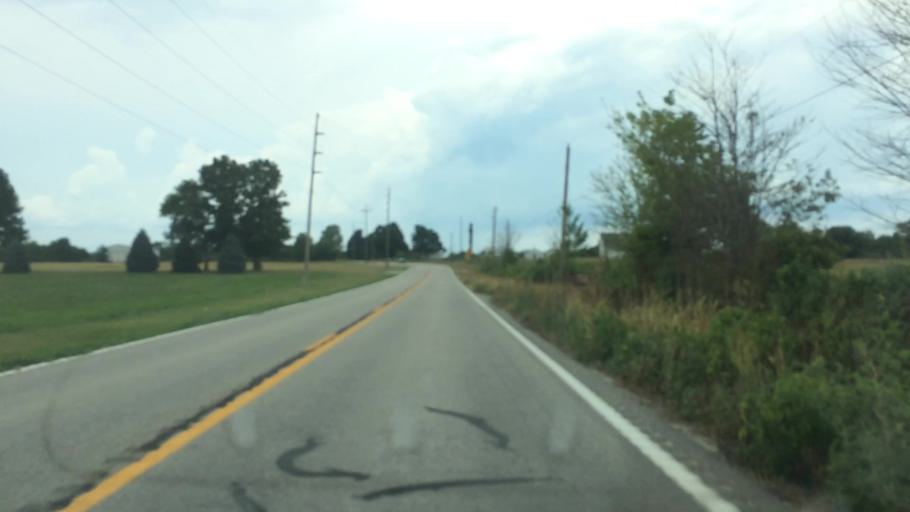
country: US
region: Missouri
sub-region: Greene County
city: Strafford
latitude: 37.2501
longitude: -93.1354
